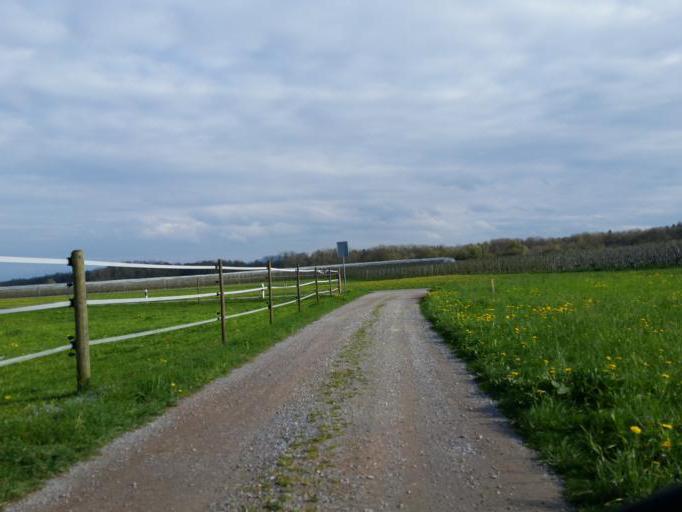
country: CH
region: Thurgau
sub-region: Arbon District
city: Uttwil
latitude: 47.5793
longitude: 9.3283
